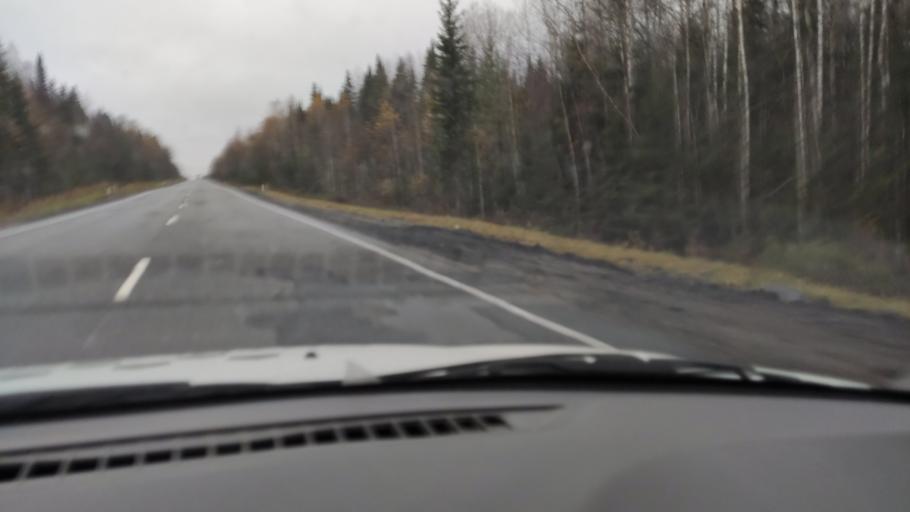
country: RU
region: Kirov
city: Omutninsk
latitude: 58.7595
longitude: 52.0164
